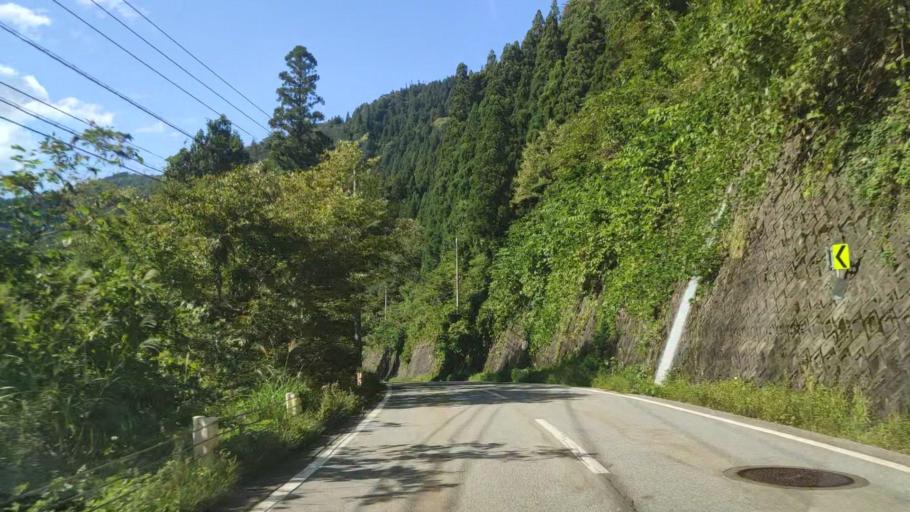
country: JP
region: Gifu
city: Takayama
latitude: 36.2950
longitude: 137.1300
